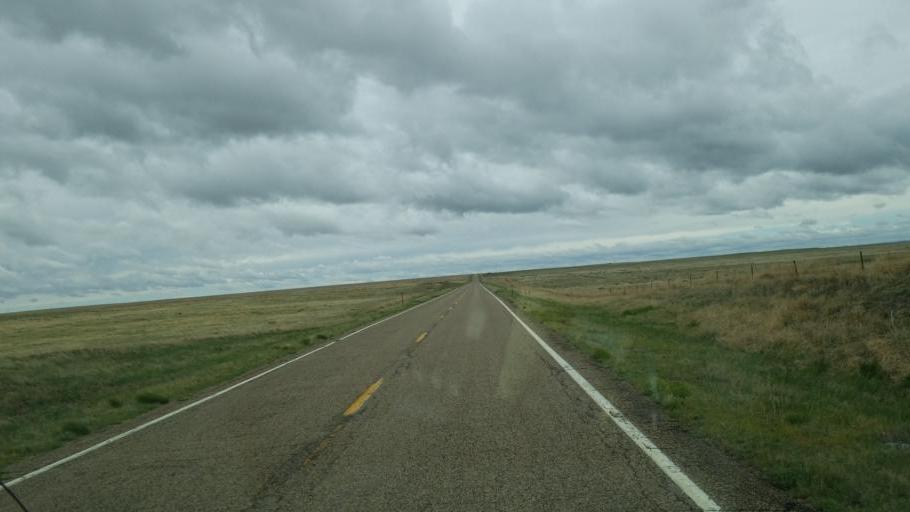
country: US
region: Colorado
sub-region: Lincoln County
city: Hugo
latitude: 38.8510
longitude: -103.6096
